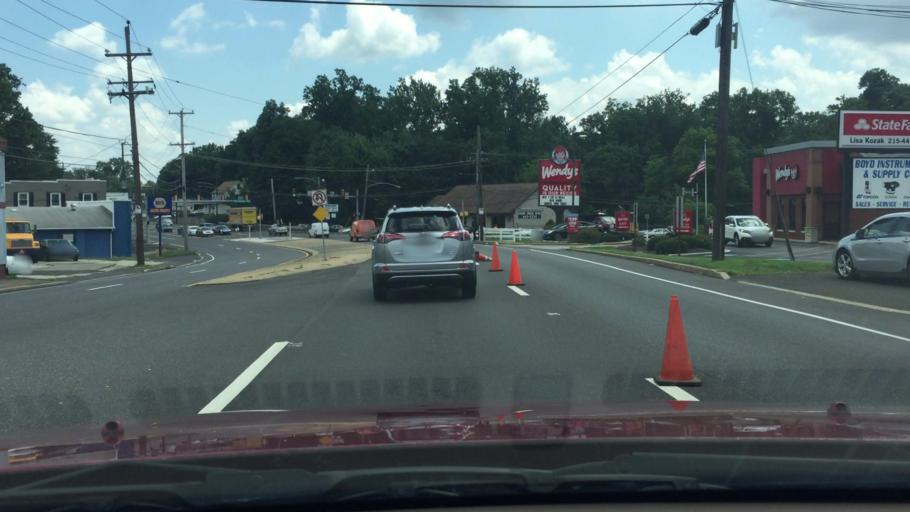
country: US
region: Pennsylvania
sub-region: Montgomery County
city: Horsham
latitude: 40.1806
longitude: -75.1308
